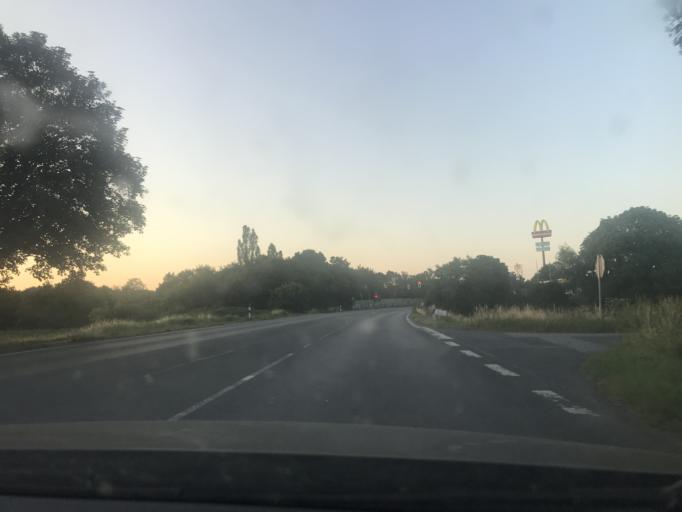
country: DE
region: North Rhine-Westphalia
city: Rheinberg
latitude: 51.5344
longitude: 6.6052
